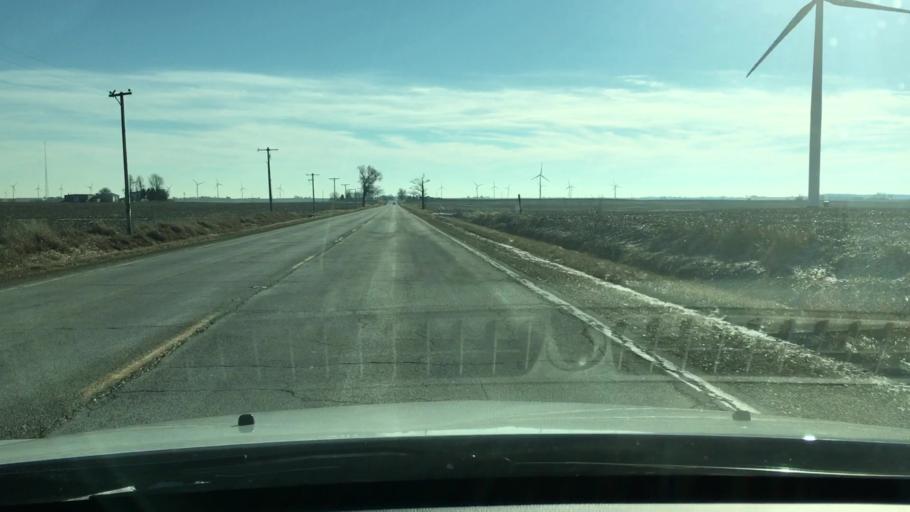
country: US
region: Illinois
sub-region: LaSalle County
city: Mendota
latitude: 41.6779
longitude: -89.1298
